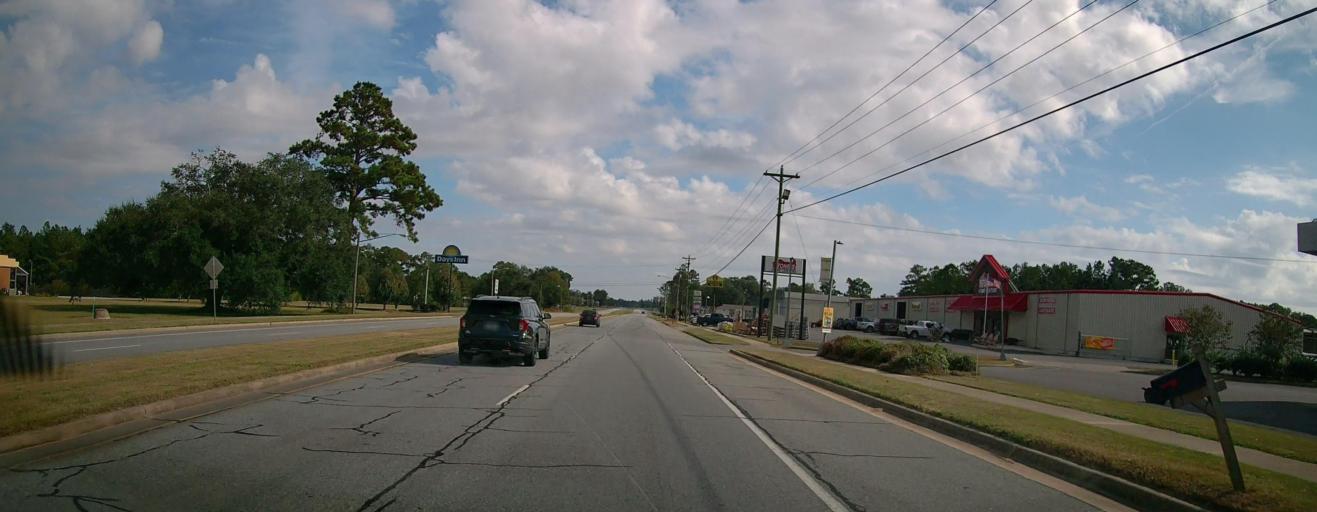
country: US
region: Georgia
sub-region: Mitchell County
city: Camilla
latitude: 31.2246
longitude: -84.1974
